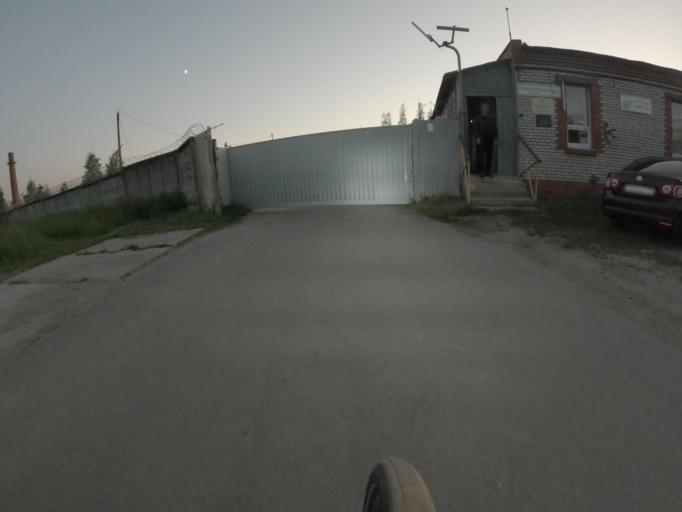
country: RU
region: St.-Petersburg
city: Sapernyy
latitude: 59.7826
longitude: 30.6742
